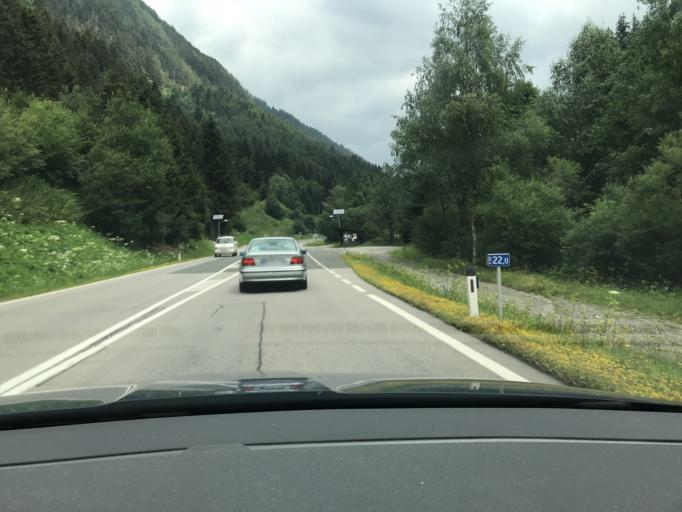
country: AT
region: Tyrol
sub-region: Politischer Bezirk Lienz
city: Hopfgarten in Defereggen
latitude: 46.9593
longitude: 12.5539
